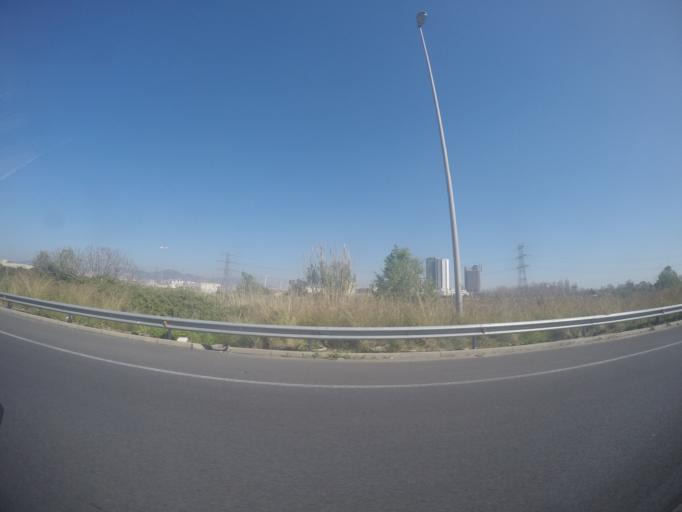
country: ES
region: Catalonia
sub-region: Provincia de Barcelona
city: El Prat de Llobregat
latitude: 41.3415
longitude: 2.0993
